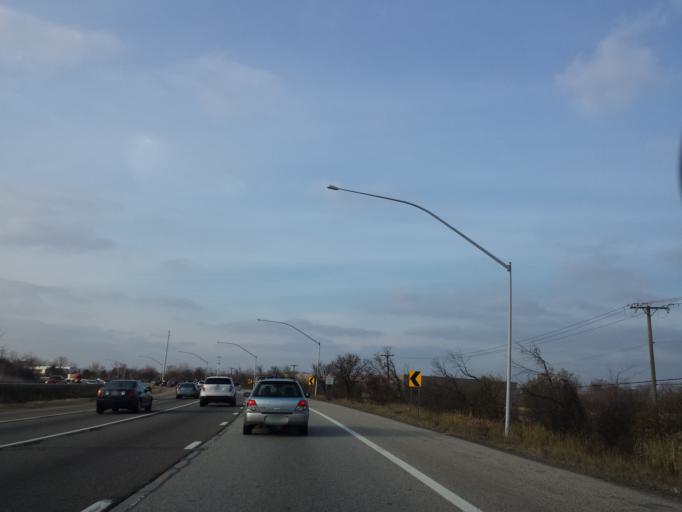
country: US
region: Michigan
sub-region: Oakland County
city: Clawson
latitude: 42.5556
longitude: -83.1175
